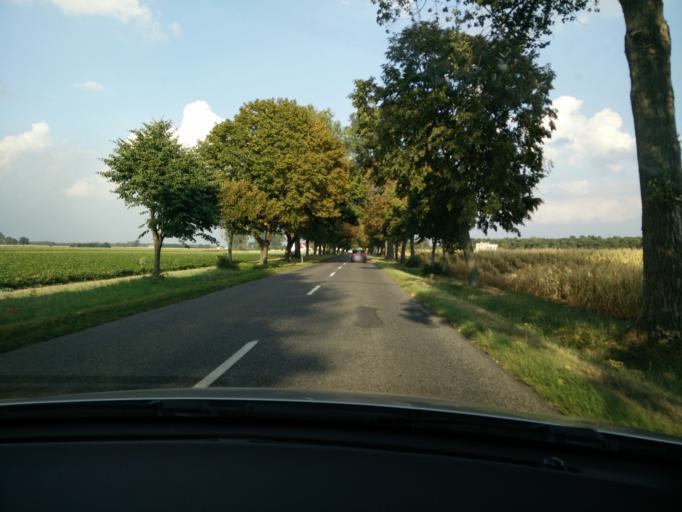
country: PL
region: Greater Poland Voivodeship
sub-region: Powiat sredzki
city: Dominowo
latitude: 52.2471
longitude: 17.3808
